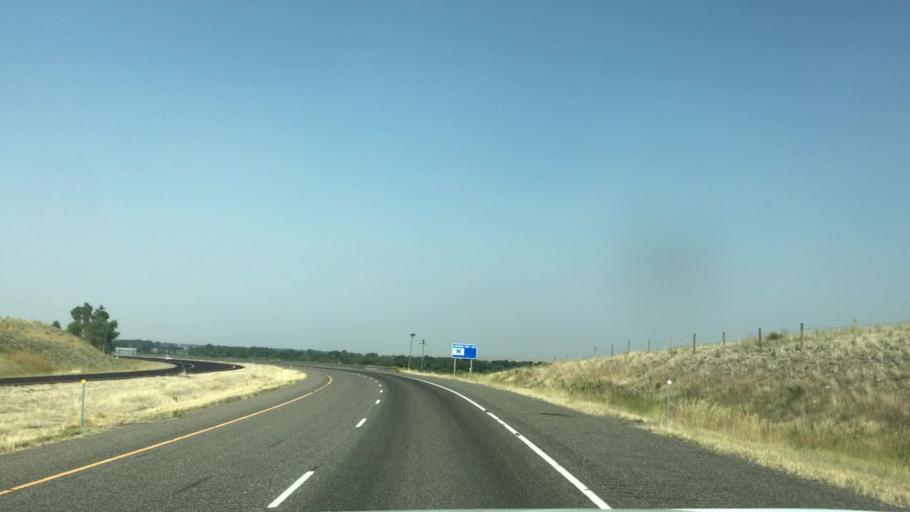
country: US
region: Montana
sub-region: Cascade County
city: Sun Prairie
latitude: 47.2479
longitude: -111.7138
